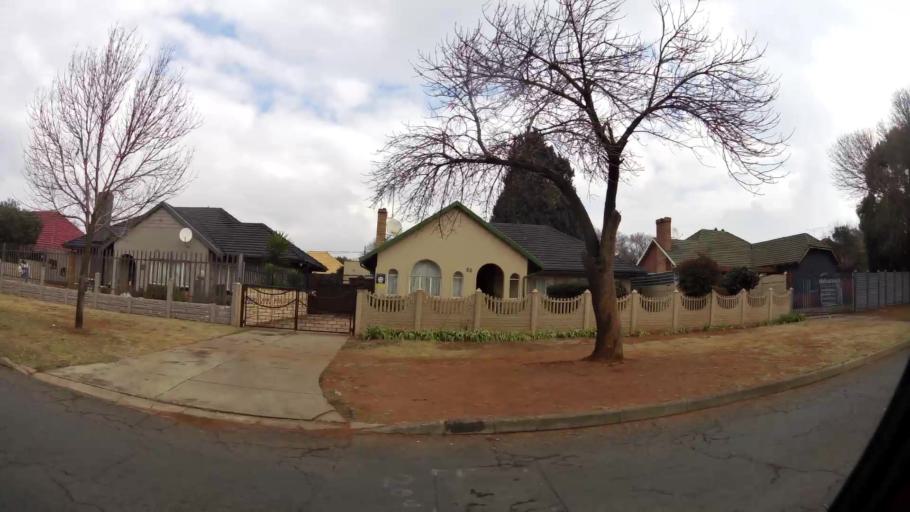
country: ZA
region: Gauteng
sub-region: Sedibeng District Municipality
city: Vanderbijlpark
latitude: -26.6984
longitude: 27.8476
